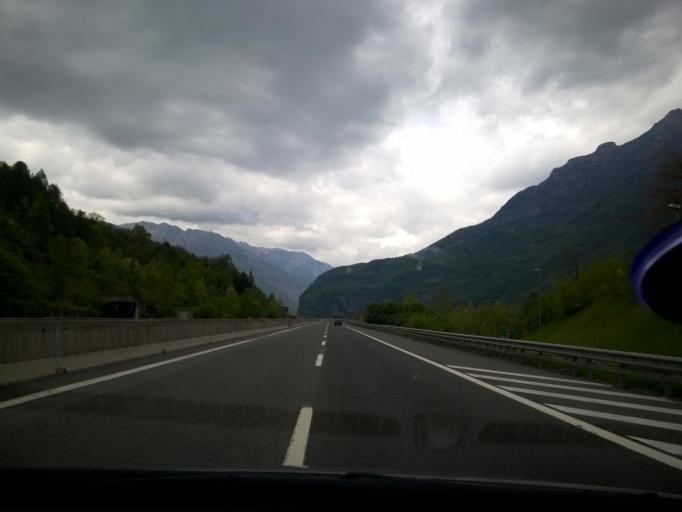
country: IT
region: Veneto
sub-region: Provincia di Belluno
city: Soccher-Paiane-Casan-Arsie
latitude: 46.1656
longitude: 12.3122
